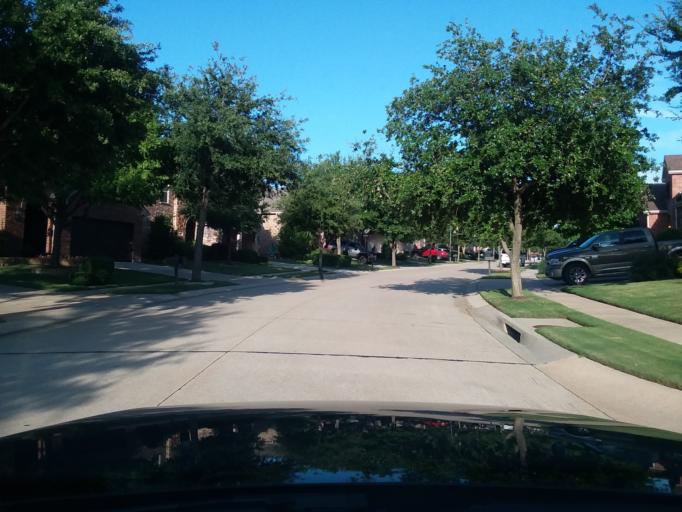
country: US
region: Texas
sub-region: Denton County
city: Copper Canyon
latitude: 33.1050
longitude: -97.1184
